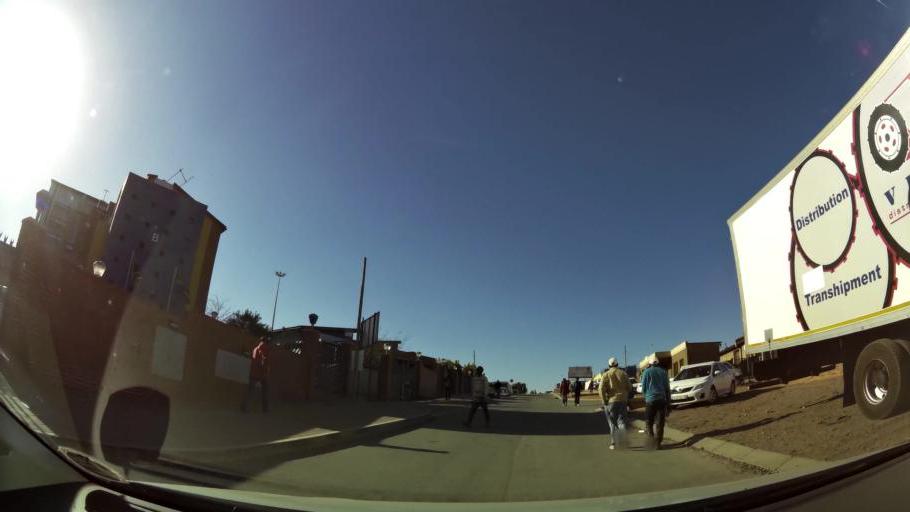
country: ZA
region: Gauteng
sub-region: Ekurhuleni Metropolitan Municipality
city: Tembisa
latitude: -26.0264
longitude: 28.2091
